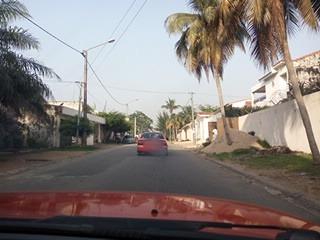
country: CI
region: Lagunes
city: Abobo
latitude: 5.3746
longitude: -3.9889
